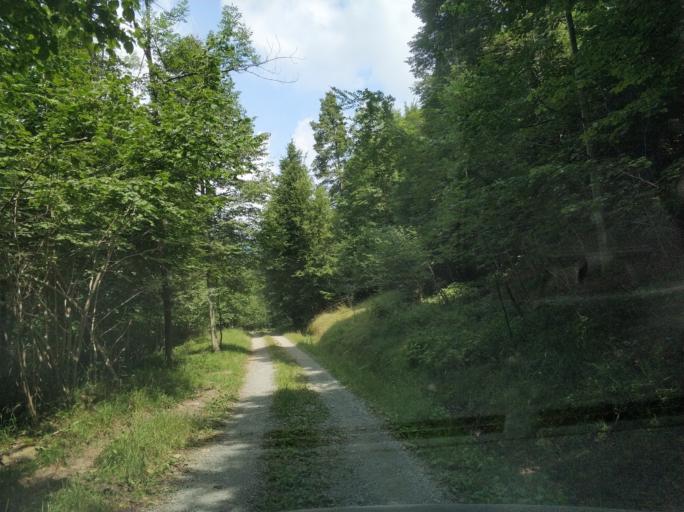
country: IT
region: Piedmont
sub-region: Provincia di Torino
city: Viu
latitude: 45.2025
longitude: 7.3932
